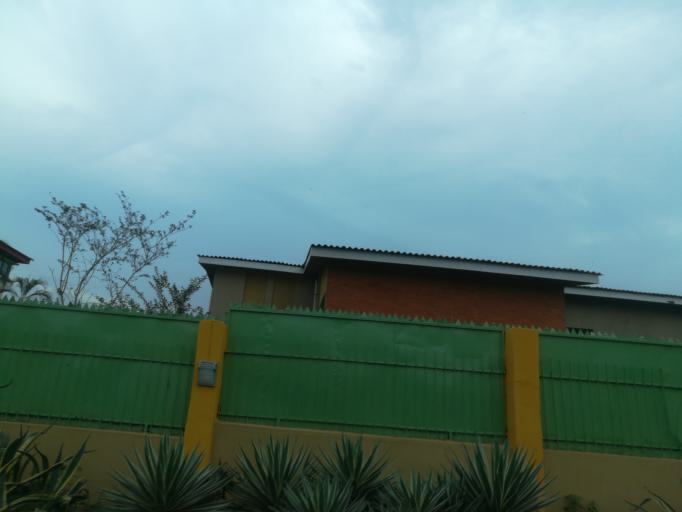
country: NG
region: Oyo
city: Ibadan
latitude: 7.4234
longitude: 3.9088
